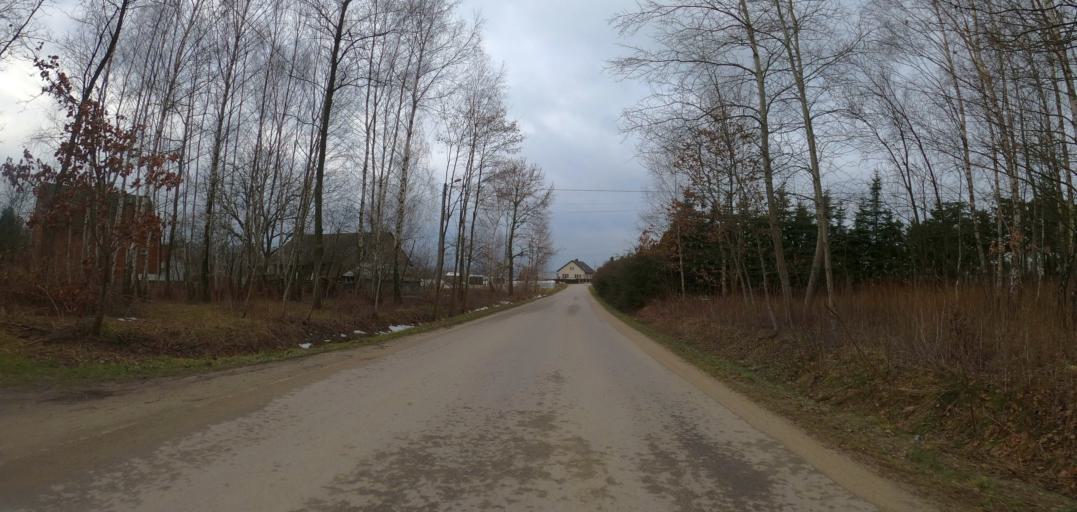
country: PL
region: Subcarpathian Voivodeship
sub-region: Powiat debicki
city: Pilzno
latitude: 49.9896
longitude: 21.3266
